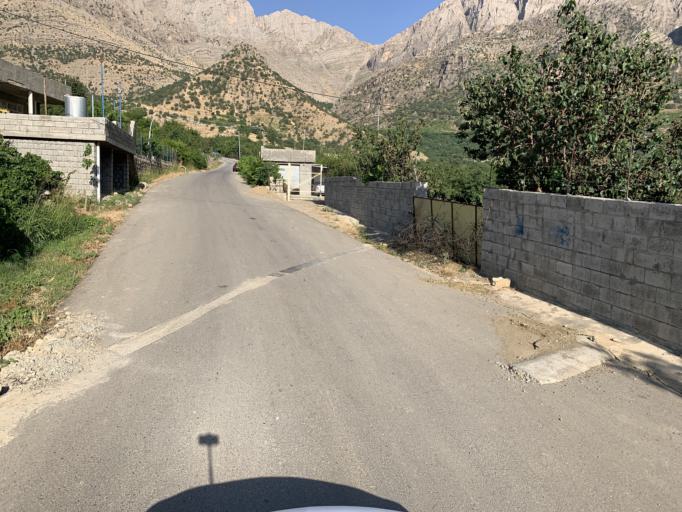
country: IQ
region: As Sulaymaniyah
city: Qeladize
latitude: 35.9919
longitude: 45.1962
